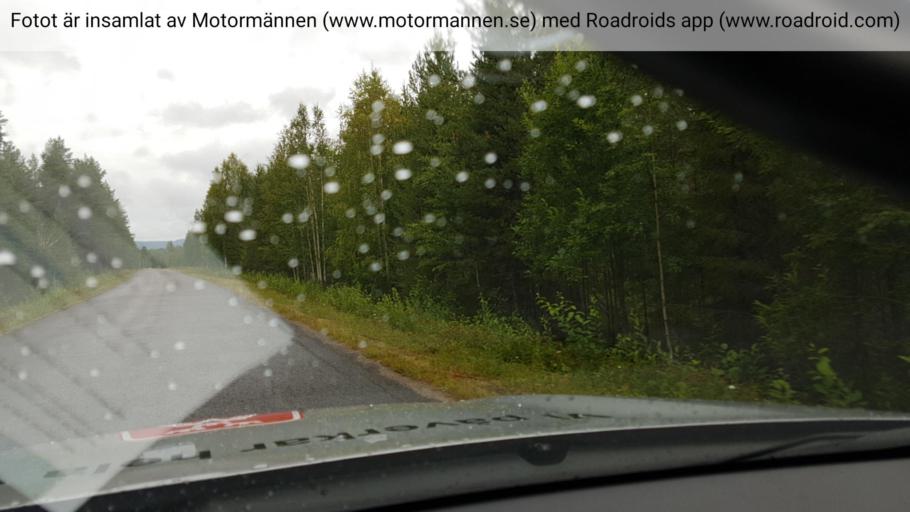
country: SE
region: Norrbotten
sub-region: Alvsbyns Kommun
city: AElvsbyn
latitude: 66.0701
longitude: 20.9361
